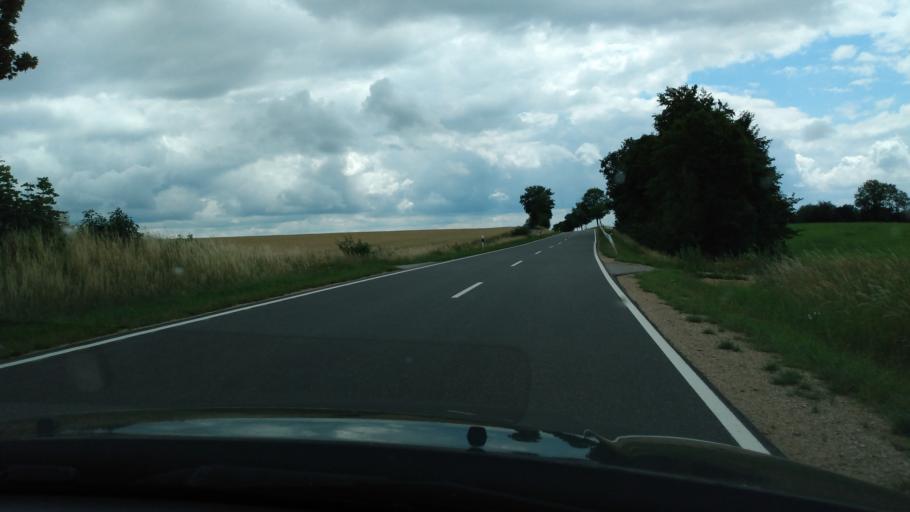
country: DE
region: Rheinland-Pfalz
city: Bleckhausen
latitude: 50.1184
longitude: 6.7822
